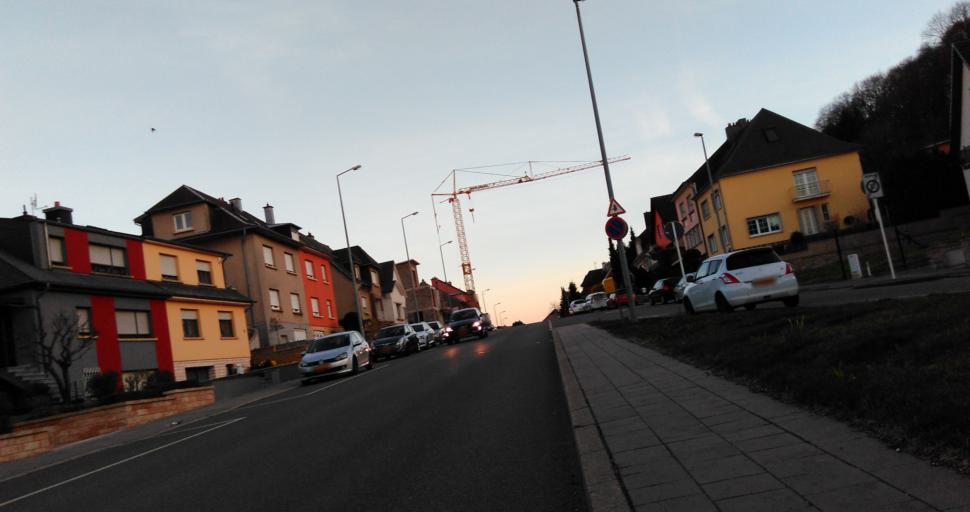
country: LU
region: Luxembourg
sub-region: Canton d'Esch-sur-Alzette
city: Niedercorn
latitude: 49.5414
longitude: 5.8901
